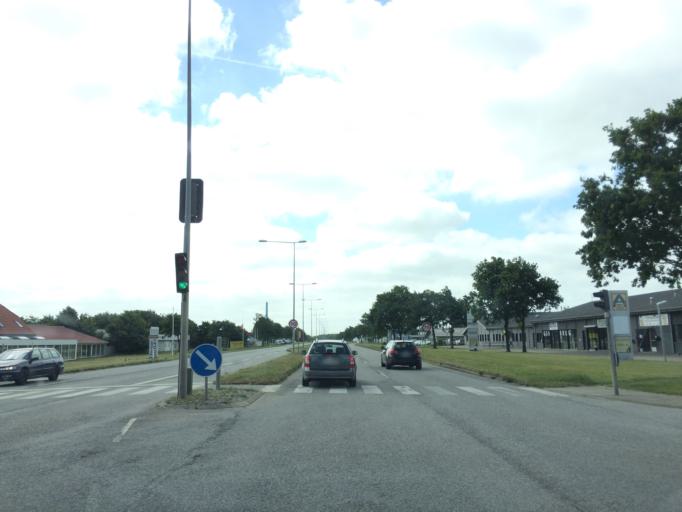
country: DK
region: Central Jutland
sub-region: Herning Kommune
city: Snejbjerg
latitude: 56.1536
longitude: 8.9312
